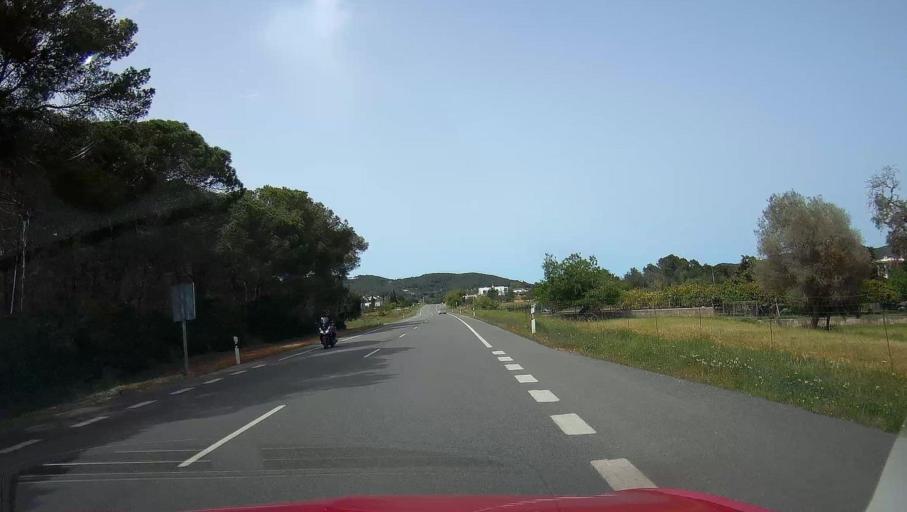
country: ES
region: Balearic Islands
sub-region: Illes Balears
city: Santa Eularia des Riu
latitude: 39.0177
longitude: 1.4874
